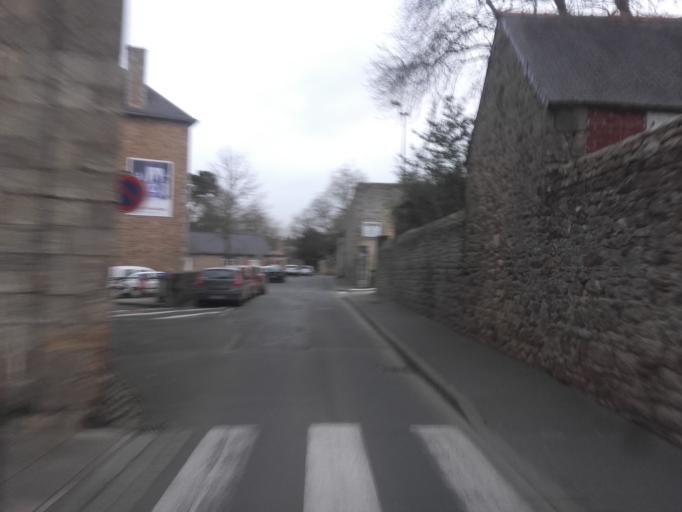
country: FR
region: Brittany
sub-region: Departement des Cotes-d'Armor
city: Guingamp
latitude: 48.5611
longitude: -3.1477
